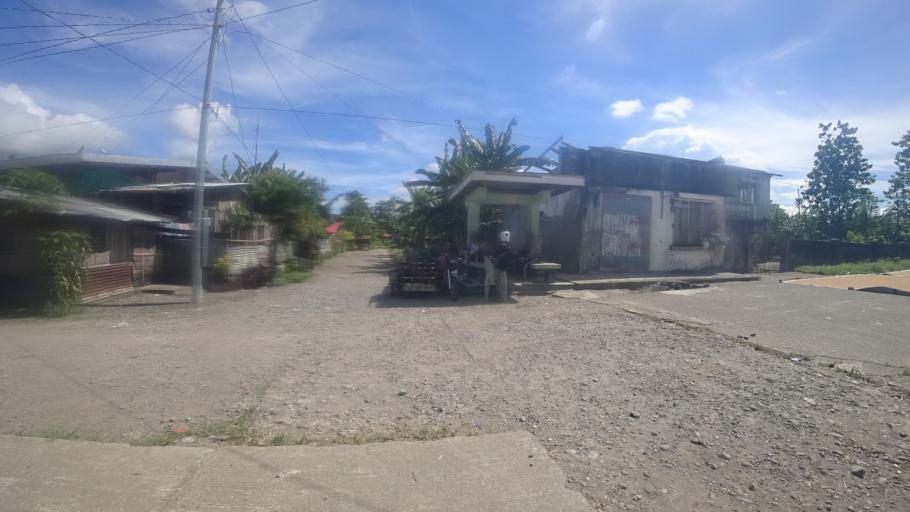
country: PH
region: Eastern Visayas
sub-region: Province of Leyte
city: Pastrana
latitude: 11.1533
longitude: 124.8597
